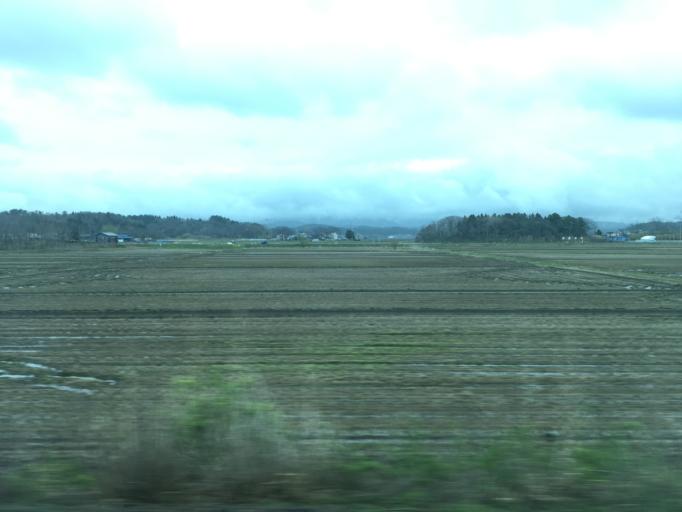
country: JP
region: Akita
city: Akita Shi
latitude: 39.8027
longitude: 140.0604
